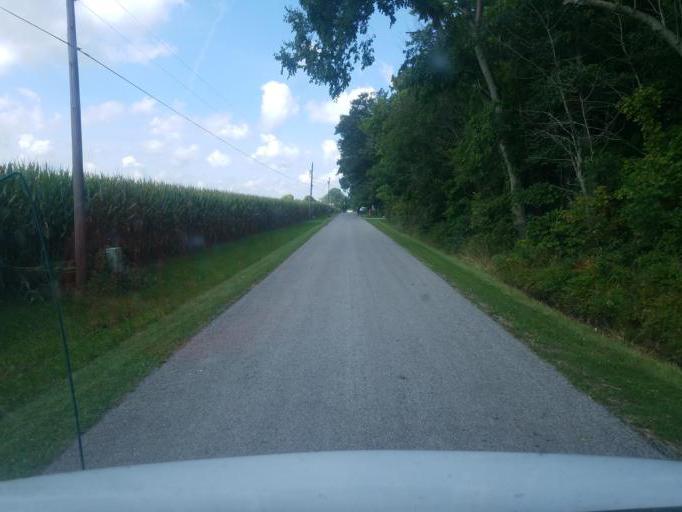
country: US
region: Ohio
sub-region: Marion County
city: Prospect
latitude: 40.4911
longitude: -83.1213
